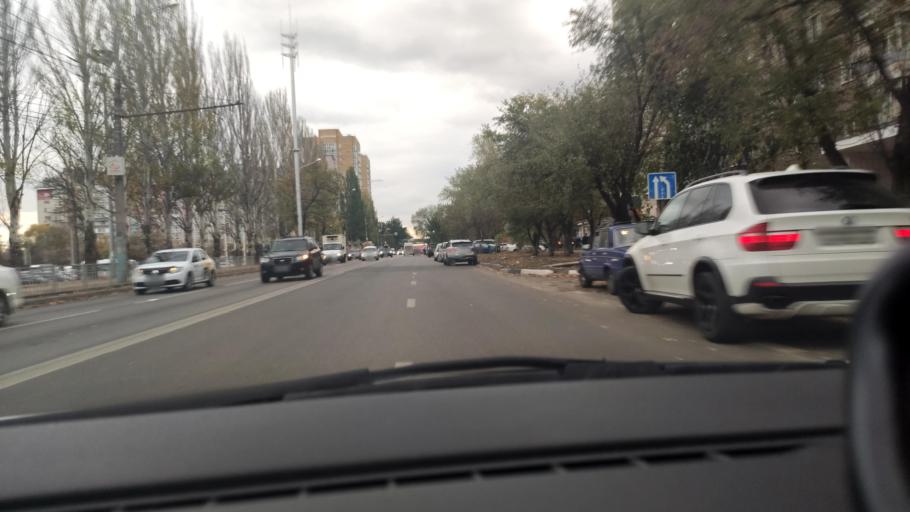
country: RU
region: Voronezj
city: Voronezh
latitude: 51.7029
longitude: 39.1959
